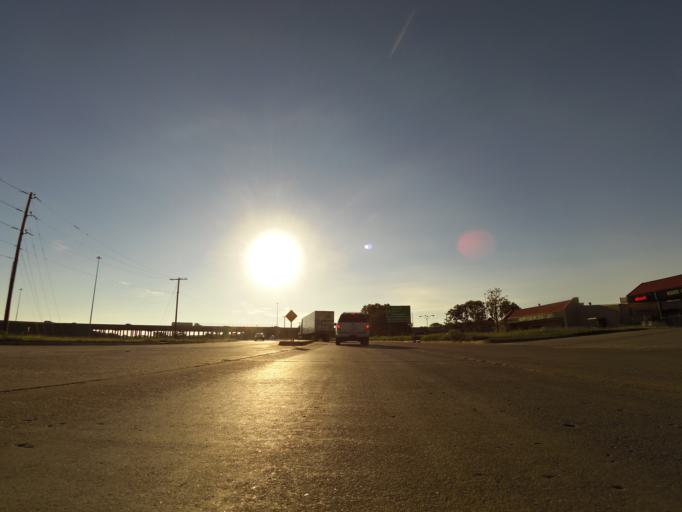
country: US
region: Kansas
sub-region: Sedgwick County
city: Wichita
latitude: 37.7374
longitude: -97.3212
